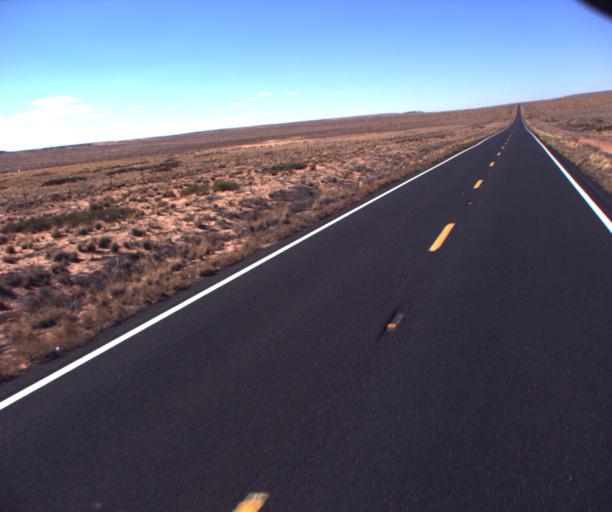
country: US
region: Arizona
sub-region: Coconino County
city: Tuba City
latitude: 36.0282
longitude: -111.1562
